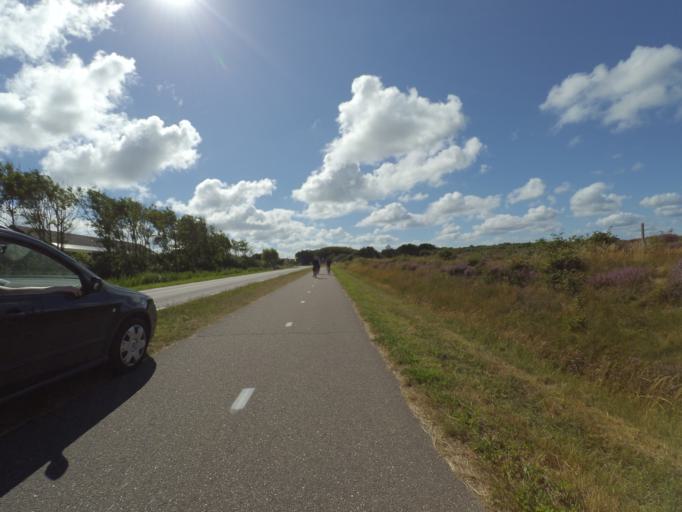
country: NL
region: North Holland
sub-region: Gemeente Texel
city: Den Burg
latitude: 53.1041
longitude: 4.7759
